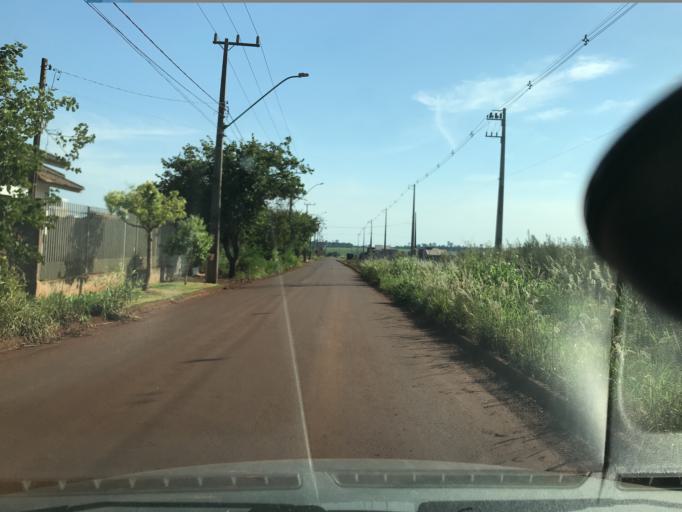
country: BR
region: Parana
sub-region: Palotina
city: Palotina
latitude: -24.2916
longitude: -53.8272
